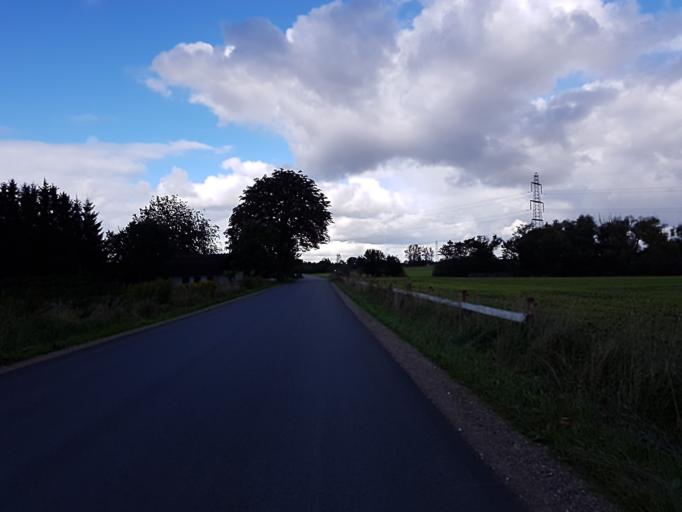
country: DK
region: Capital Region
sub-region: Egedal Kommune
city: Vekso
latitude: 55.7347
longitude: 12.2112
